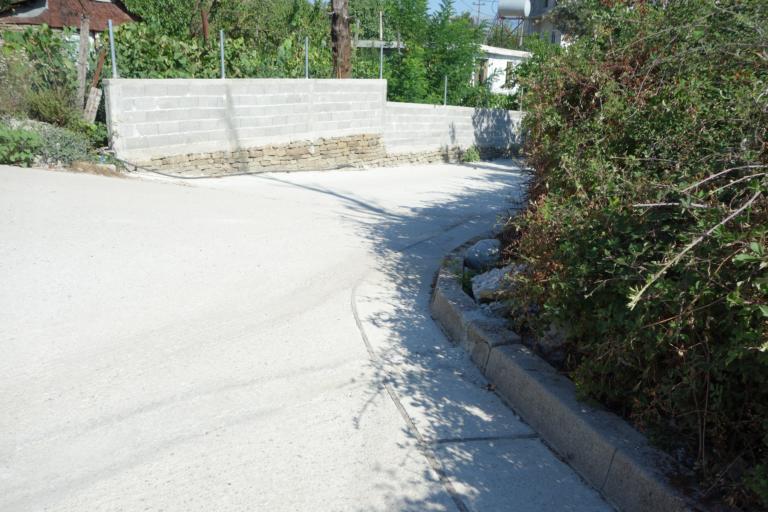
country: AL
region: Gjirokaster
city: Gjirokaster
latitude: 40.0873
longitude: 20.1390
